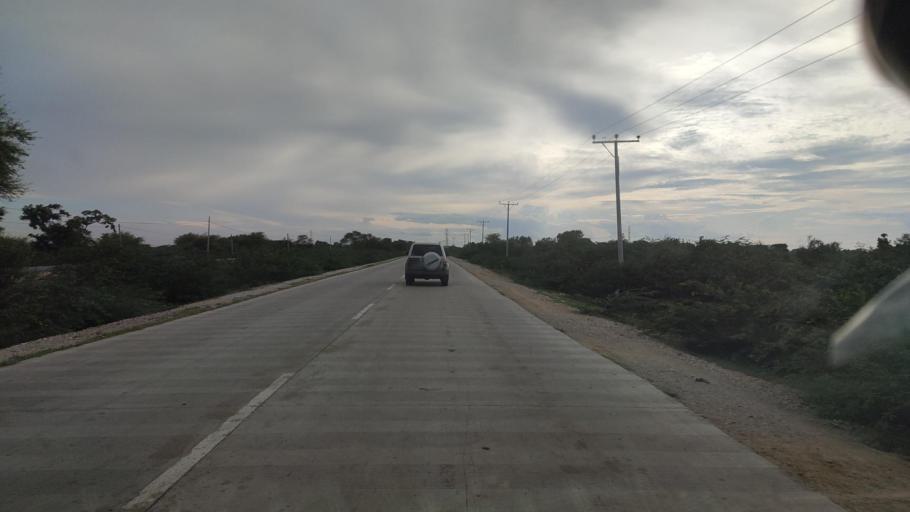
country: MM
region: Mandalay
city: Kyaukse
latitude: 21.3473
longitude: 96.1051
